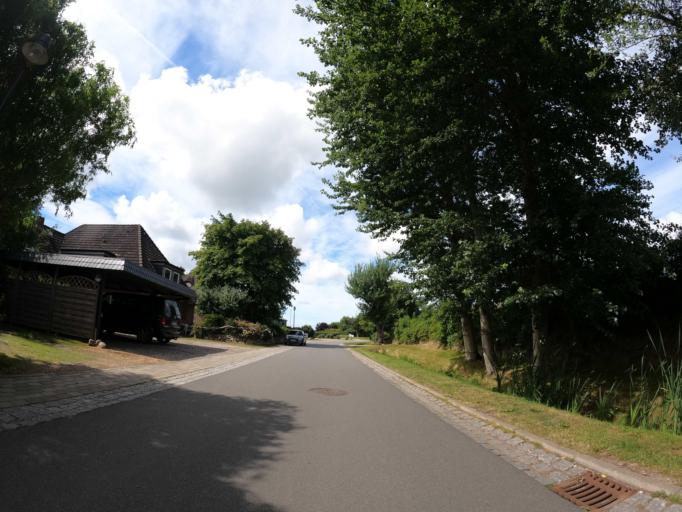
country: DE
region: Schleswig-Holstein
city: Sylt-Ost
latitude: 54.8734
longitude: 8.4294
